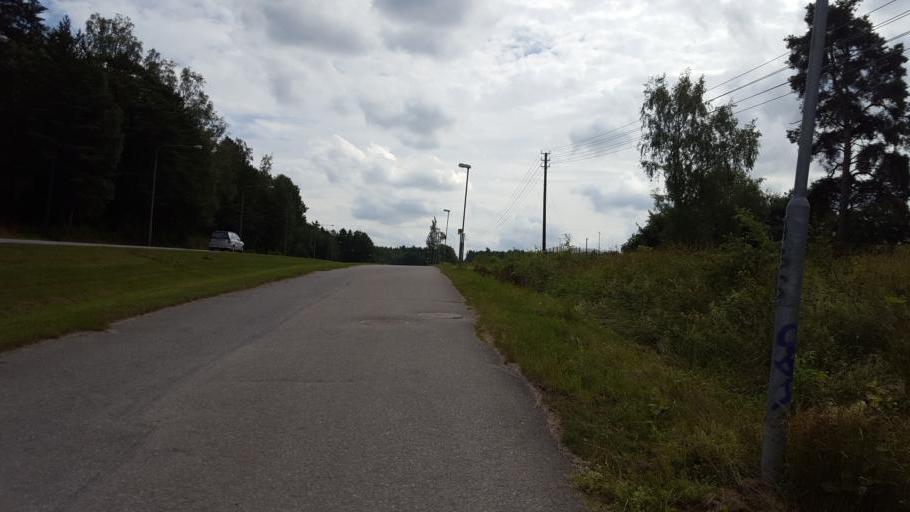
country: SE
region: Stockholm
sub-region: Upplands Vasby Kommun
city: Upplands Vaesby
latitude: 59.5120
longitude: 17.8990
